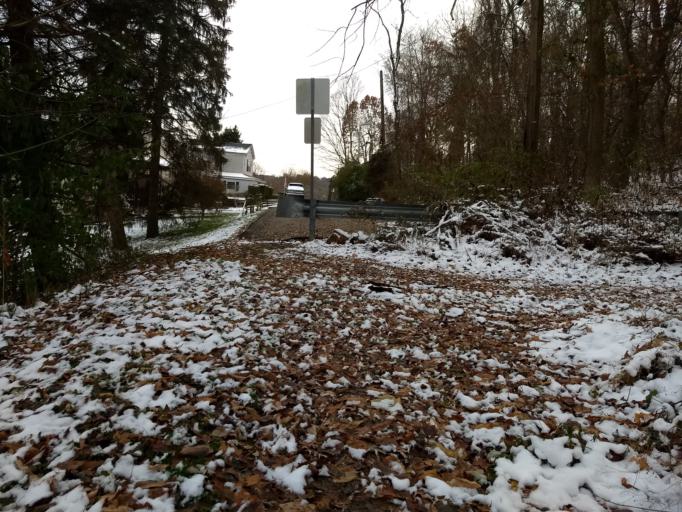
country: US
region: Pennsylvania
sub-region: Allegheny County
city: Mount Oliver
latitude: 40.4046
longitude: -80.0043
